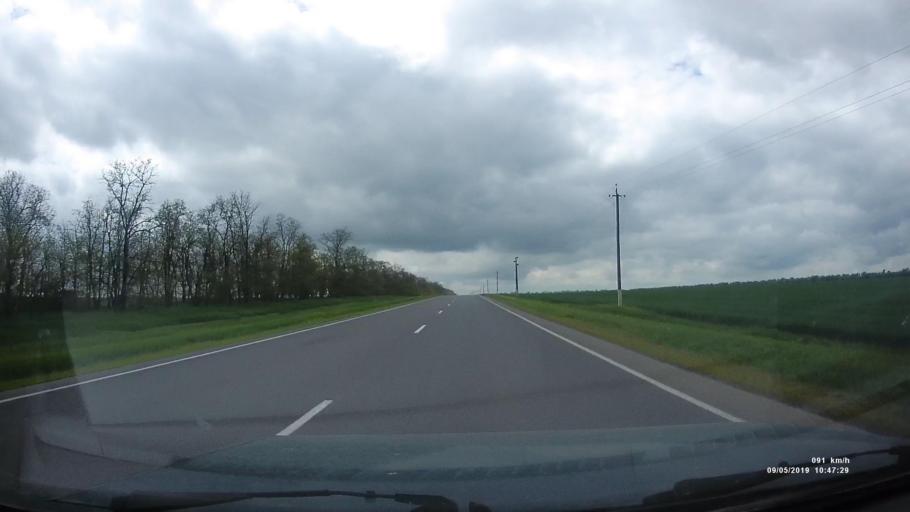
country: RU
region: Rostov
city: Peshkovo
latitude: 46.9699
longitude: 39.3556
